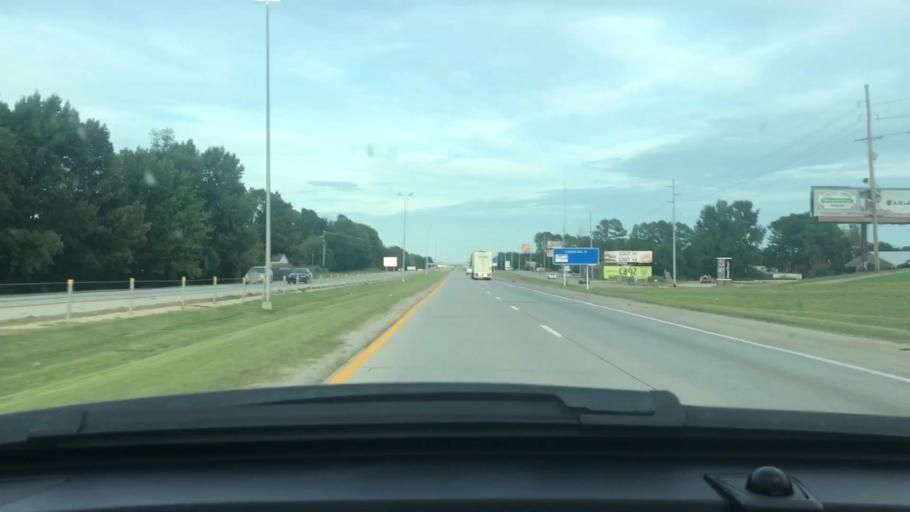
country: US
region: Arkansas
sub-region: Craighead County
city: Jonesboro
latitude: 35.8072
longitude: -90.7108
